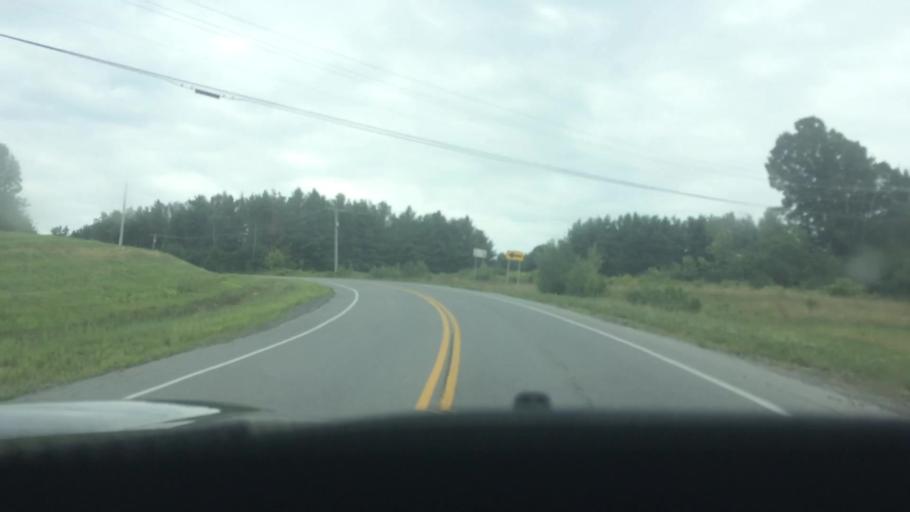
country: US
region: New York
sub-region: St. Lawrence County
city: Canton
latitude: 44.5422
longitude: -75.0994
